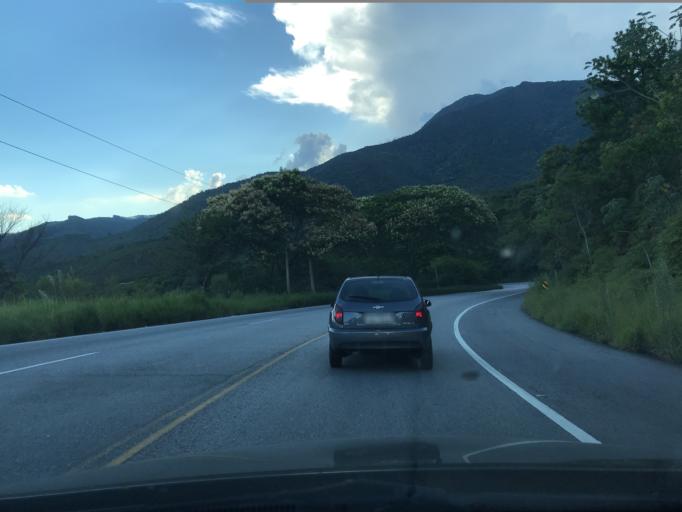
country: BR
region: Sao Paulo
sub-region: Campos Do Jordao
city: Campos do Jordao
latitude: -22.8556
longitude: -45.6197
